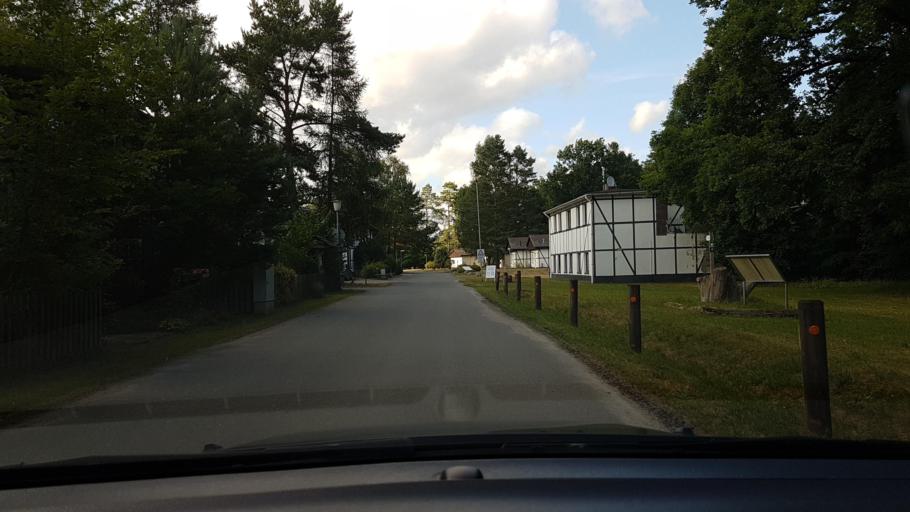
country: DE
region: Lower Saxony
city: Fassberg
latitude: 52.8736
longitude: 10.2267
